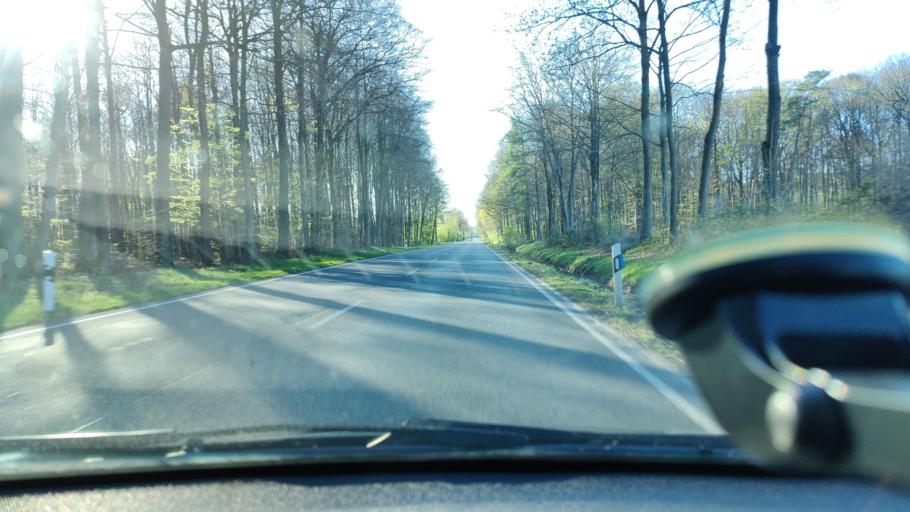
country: DE
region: North Rhine-Westphalia
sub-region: Regierungsbezirk Munster
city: Ahaus
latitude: 52.0566
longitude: 7.0461
